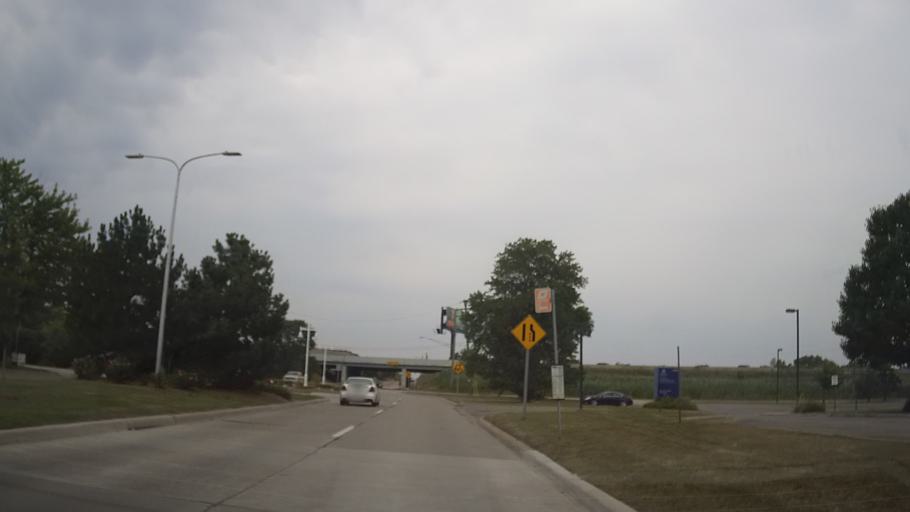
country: US
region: Michigan
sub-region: Macomb County
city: Saint Clair Shores
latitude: 42.5325
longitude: -82.9029
